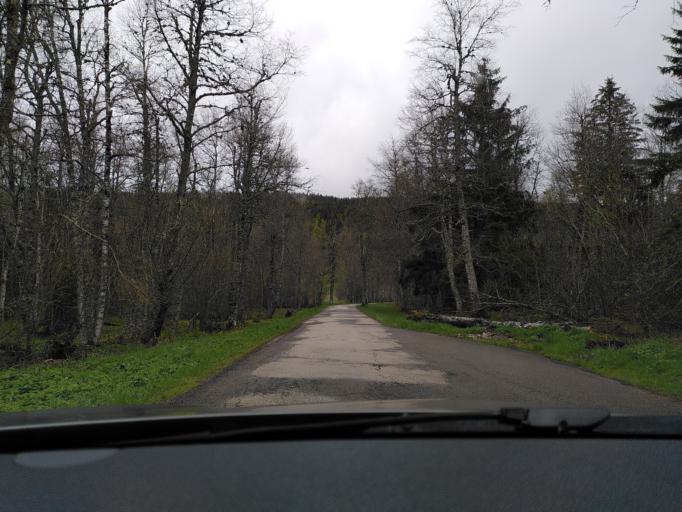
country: FR
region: Franche-Comte
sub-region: Departement du Jura
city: Les Rousses
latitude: 46.5152
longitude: 6.1091
